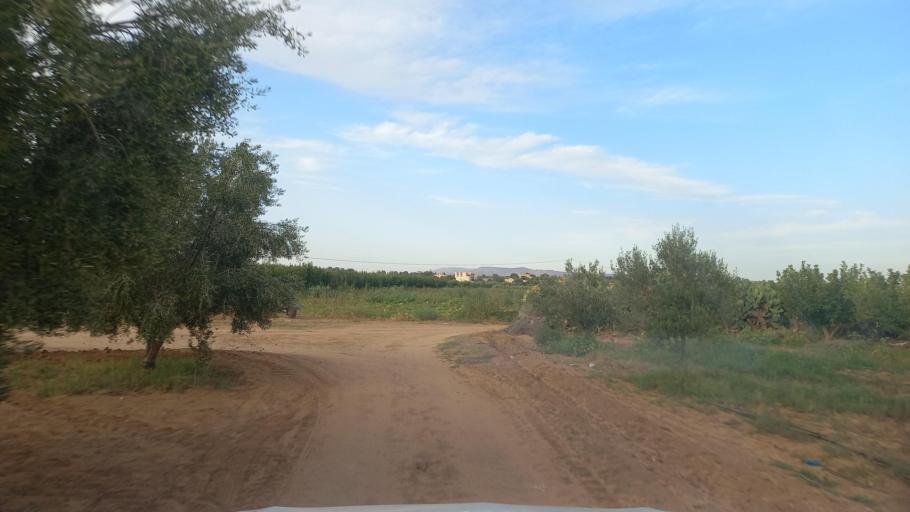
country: TN
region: Al Qasrayn
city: Kasserine
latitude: 35.2535
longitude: 9.0398
